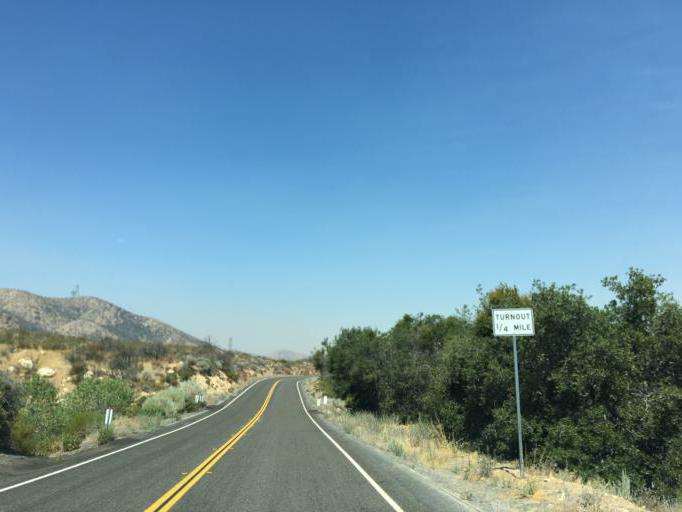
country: US
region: California
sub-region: Los Angeles County
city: Vincent
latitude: 34.4300
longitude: -118.1211
